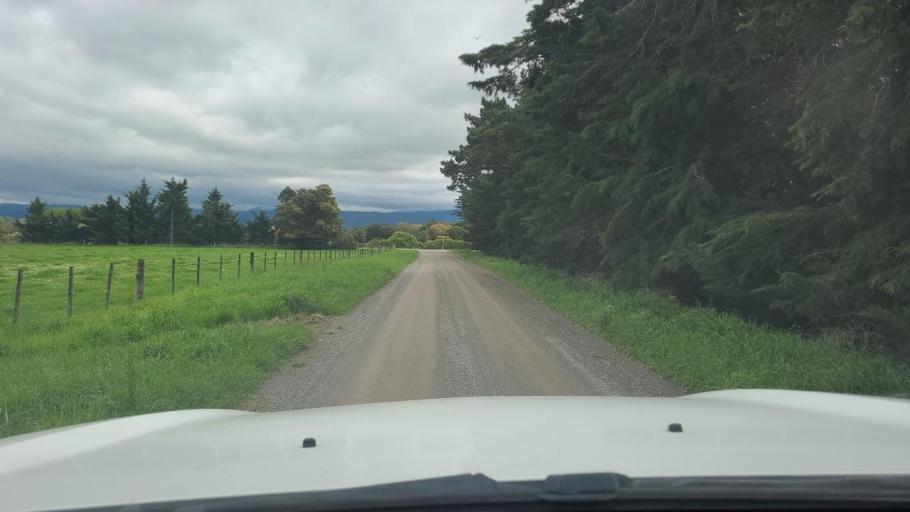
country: NZ
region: Wellington
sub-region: South Wairarapa District
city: Waipawa
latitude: -41.1437
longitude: 175.3959
